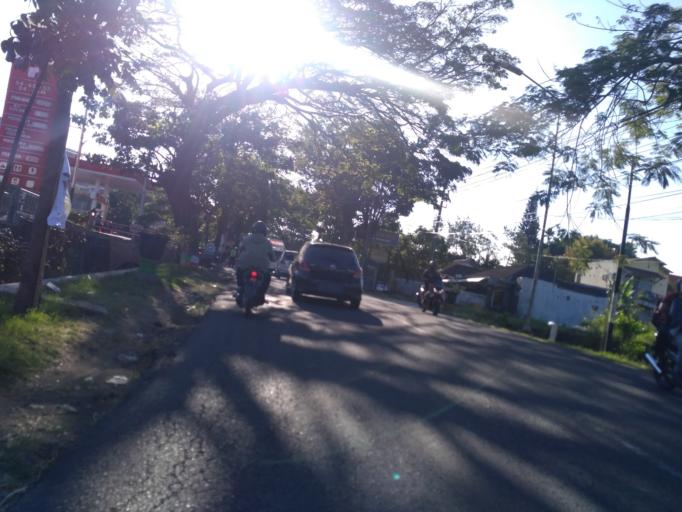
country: ID
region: East Java
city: Batu
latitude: -7.8974
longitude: 112.5562
